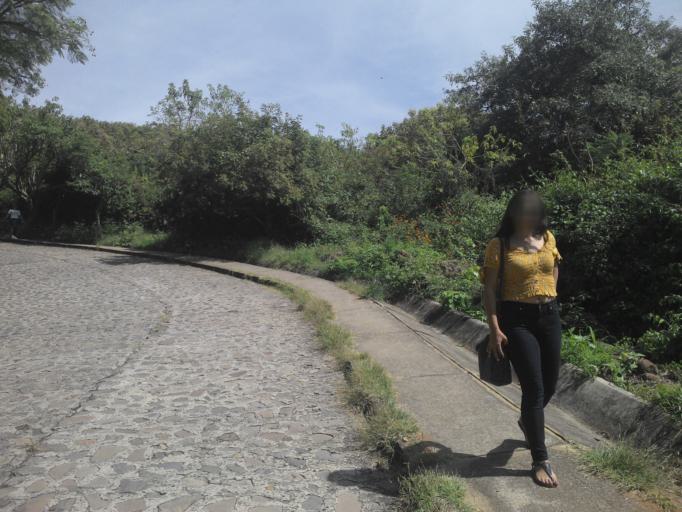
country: MX
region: Jalisco
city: Teuchitlan
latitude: 20.6946
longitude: -103.8387
